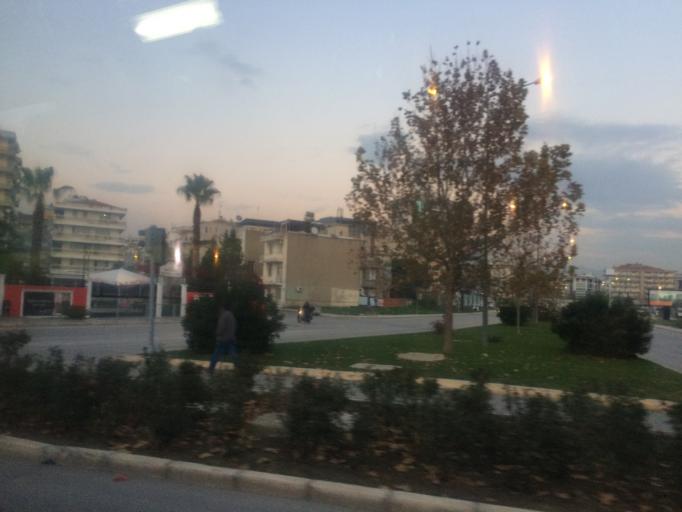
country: TR
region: Izmir
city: Karsiyaka
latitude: 38.4643
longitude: 27.0958
